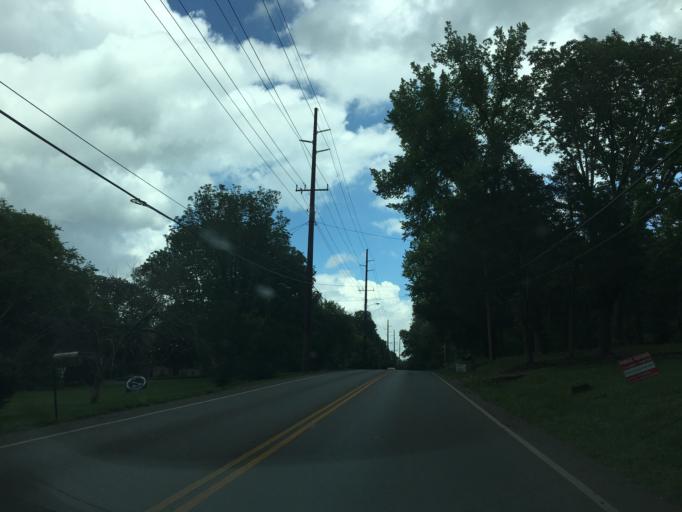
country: US
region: Tennessee
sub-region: Davidson County
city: Belle Meade
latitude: 36.0929
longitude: -86.8434
